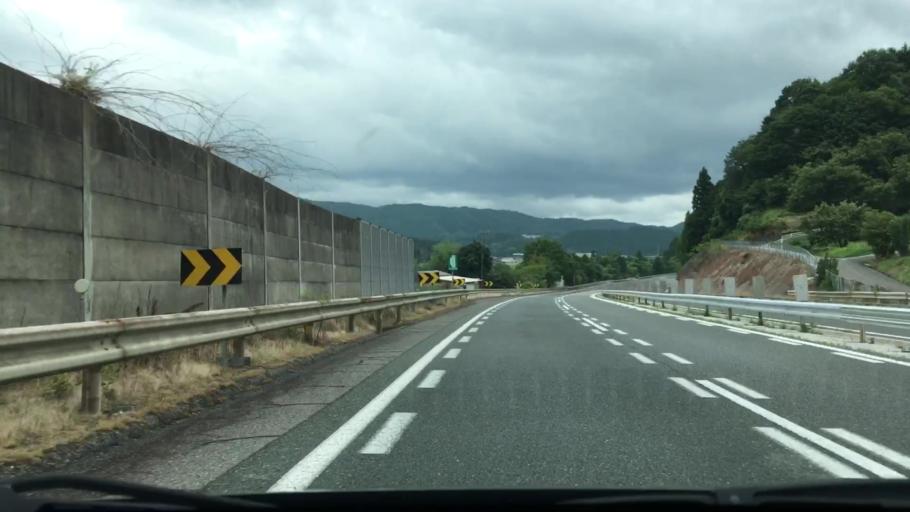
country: JP
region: Okayama
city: Niimi
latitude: 34.9493
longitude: 133.3298
